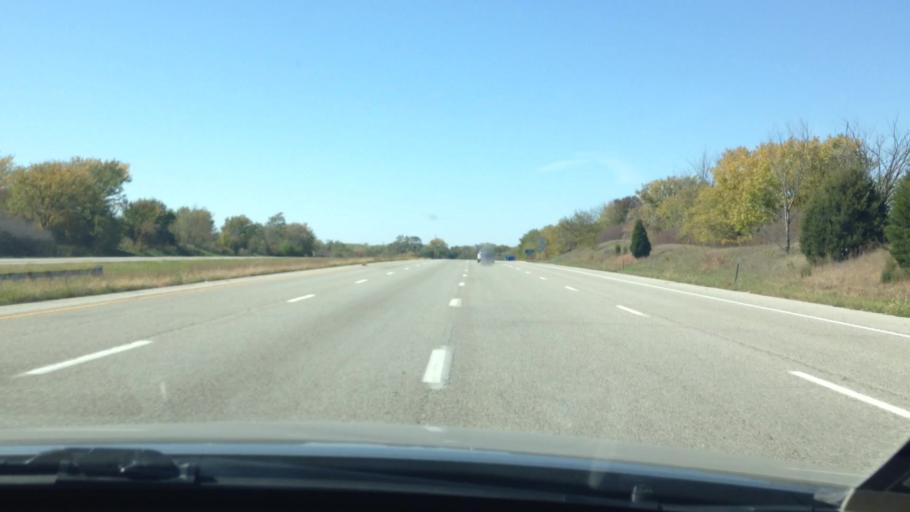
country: US
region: Missouri
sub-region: Platte County
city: Weatherby Lake
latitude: 39.3077
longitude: -94.6591
